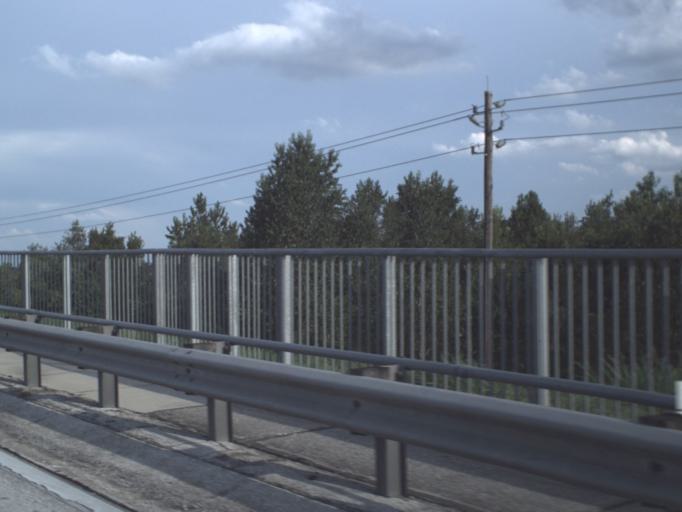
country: US
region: Florida
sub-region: Polk County
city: Lakeland
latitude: 28.0548
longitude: -81.9724
